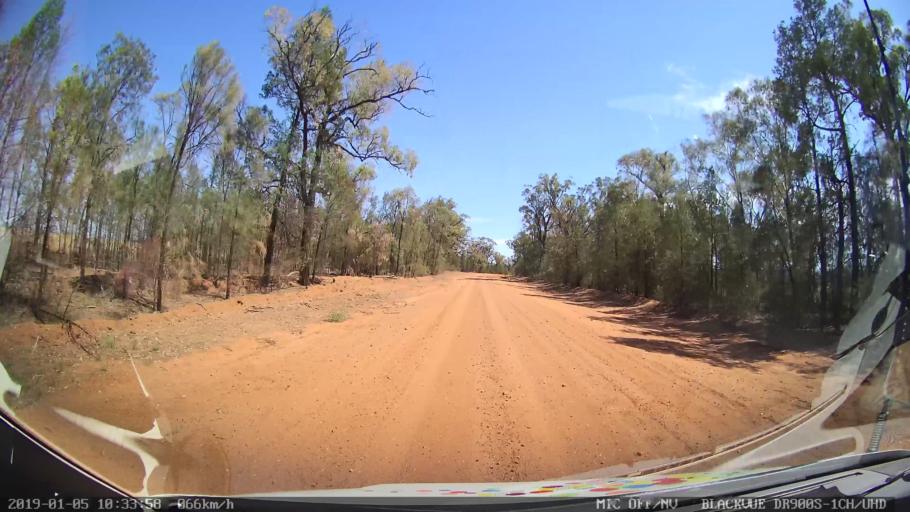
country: AU
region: New South Wales
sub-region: Gilgandra
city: Gilgandra
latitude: -31.5023
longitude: 148.9293
